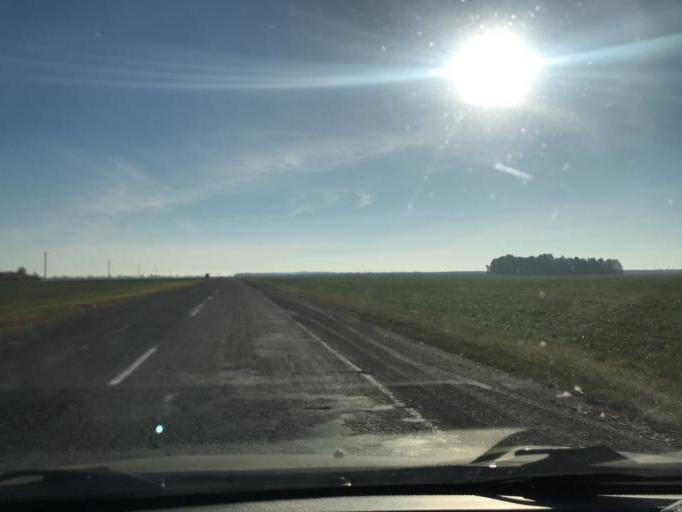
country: BY
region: Gomel
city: Brahin
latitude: 51.7933
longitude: 30.1642
